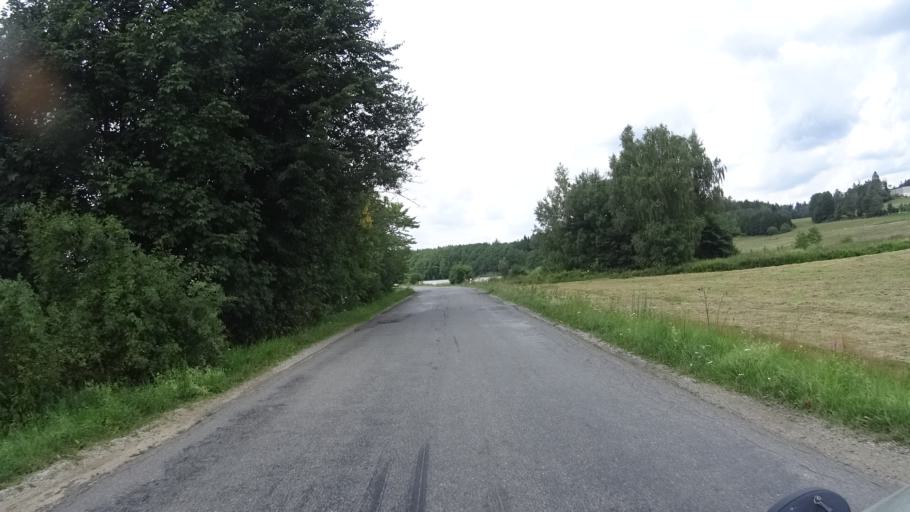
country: CZ
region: Vysocina
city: Merin
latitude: 49.4113
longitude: 15.9416
